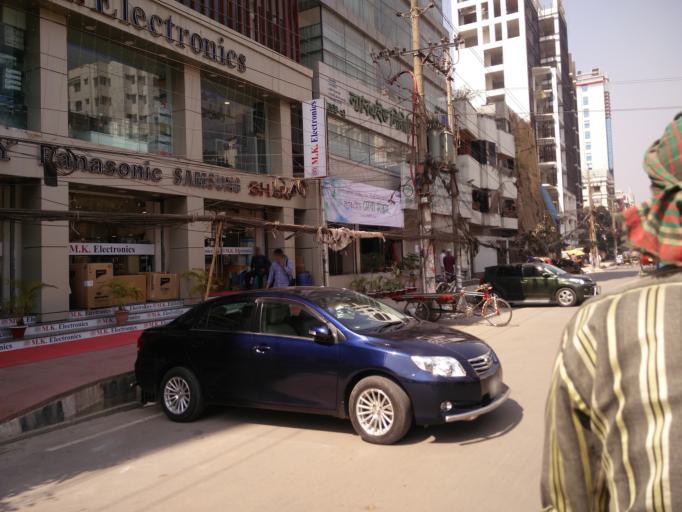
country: BD
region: Dhaka
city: Tungi
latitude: 23.8723
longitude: 90.3909
